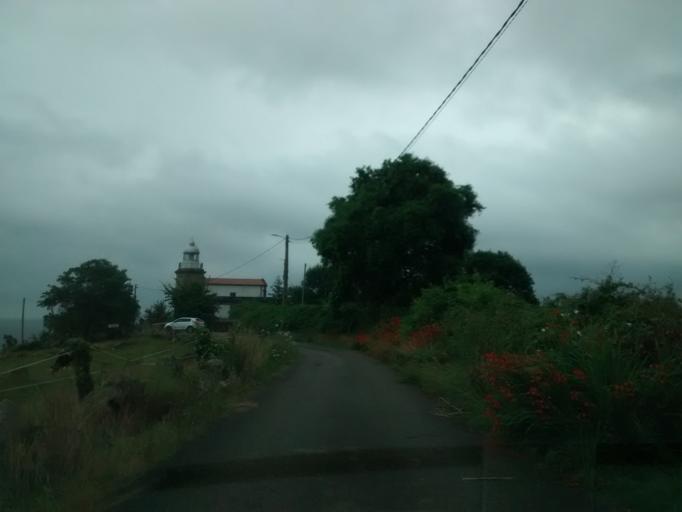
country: ES
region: Asturias
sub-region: Province of Asturias
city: Villaviciosa
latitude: 43.5480
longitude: -5.4004
